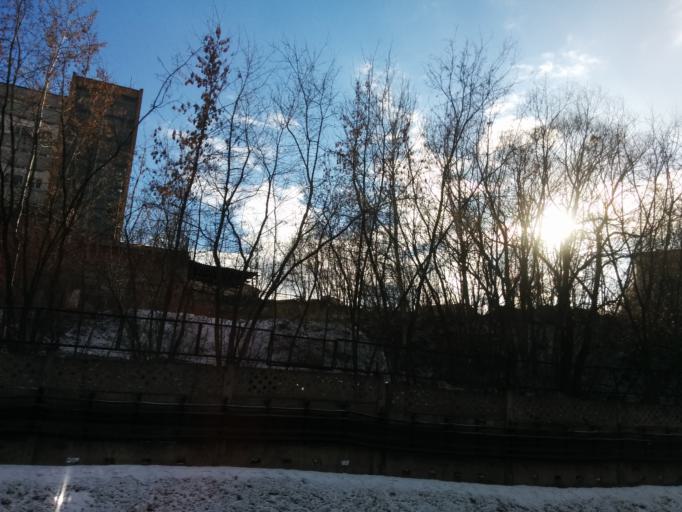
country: RU
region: Moskovskaya
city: Presnenskiy
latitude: 55.7438
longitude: 37.5261
